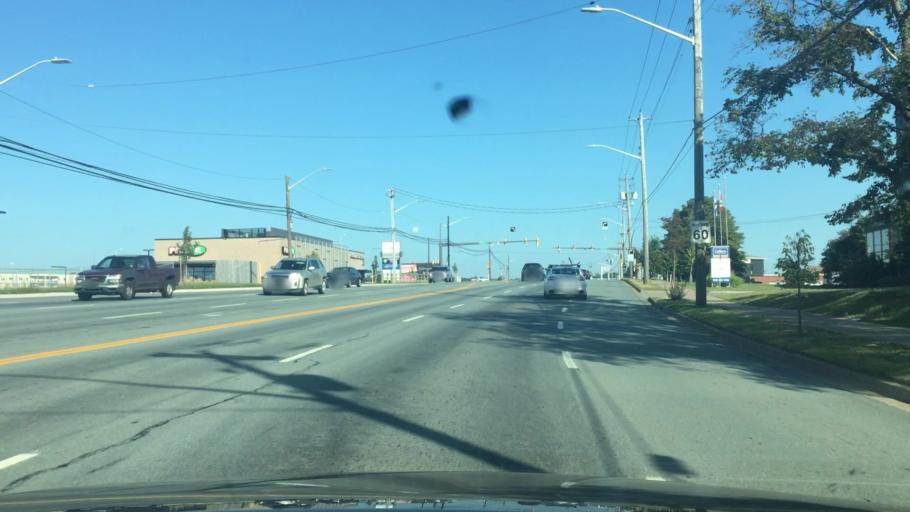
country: CA
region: Nova Scotia
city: Dartmouth
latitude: 44.6994
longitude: -63.6061
